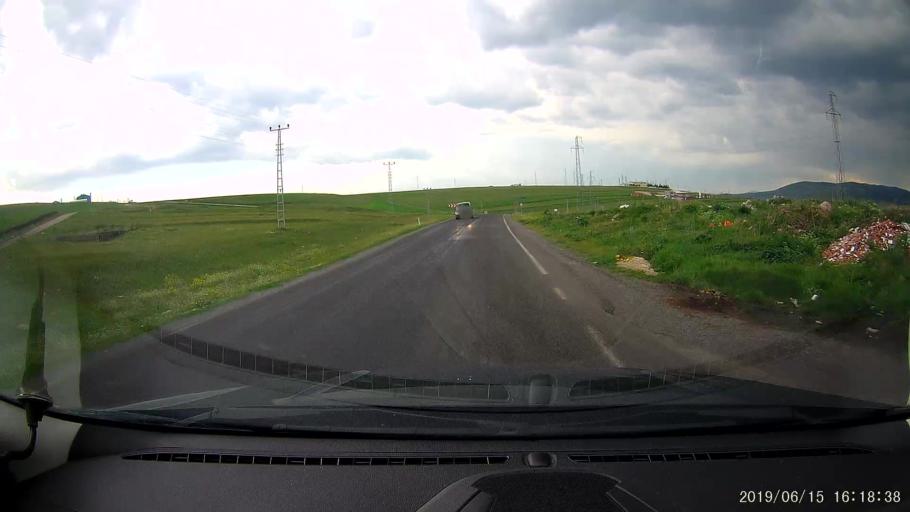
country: TR
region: Ardahan
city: Hanak
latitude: 41.2374
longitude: 42.8524
